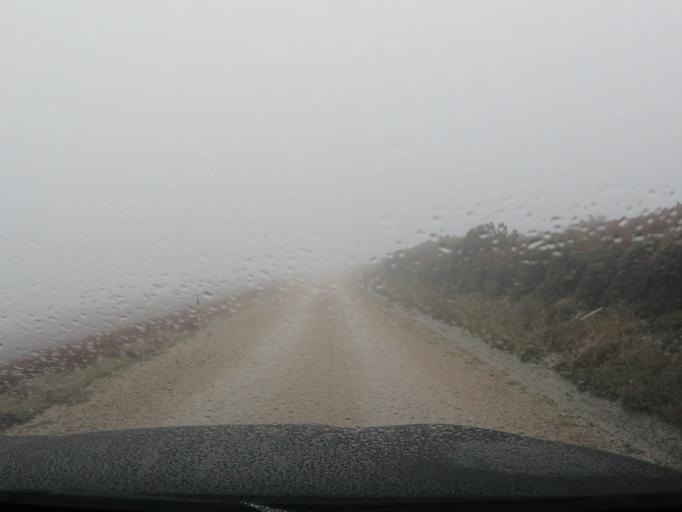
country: PT
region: Vila Real
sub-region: Vila Real
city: Vila Real
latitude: 41.3259
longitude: -7.8335
